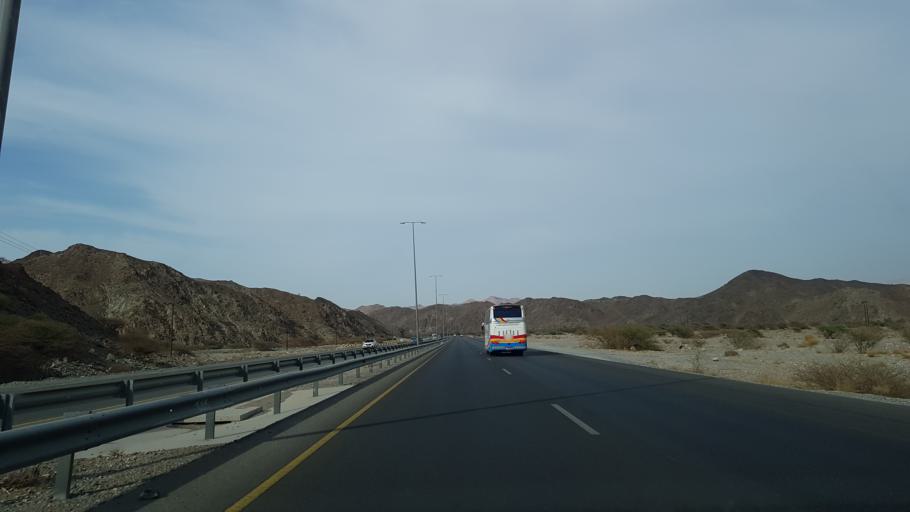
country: OM
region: Muhafazat ad Dakhiliyah
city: Bidbid
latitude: 23.3970
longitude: 58.0726
